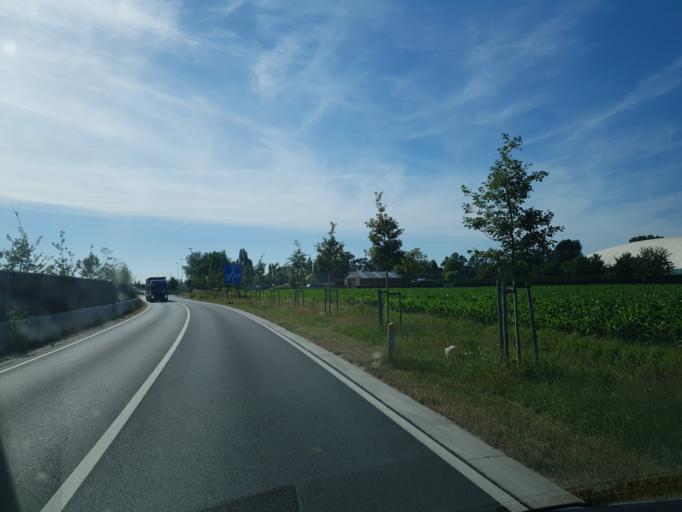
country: BE
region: Flanders
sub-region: Provincie Antwerpen
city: Brecht
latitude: 51.3577
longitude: 4.6444
